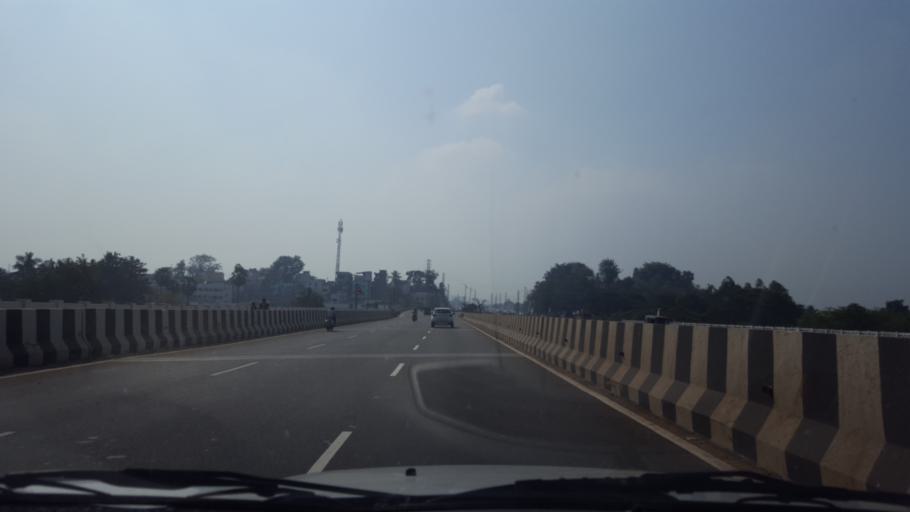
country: IN
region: Andhra Pradesh
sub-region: Vishakhapatnam
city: Bhimunipatnam
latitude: 17.9384
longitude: 83.4219
